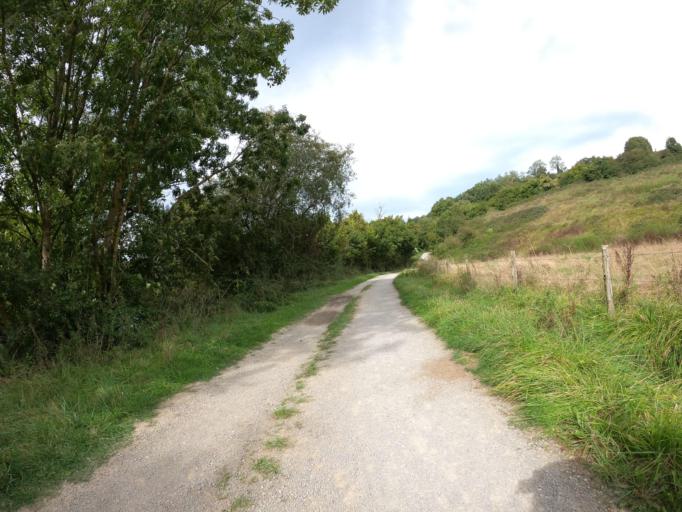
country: ES
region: Navarre
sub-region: Provincia de Navarra
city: Lekunberri
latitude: 42.9937
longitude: -1.8900
